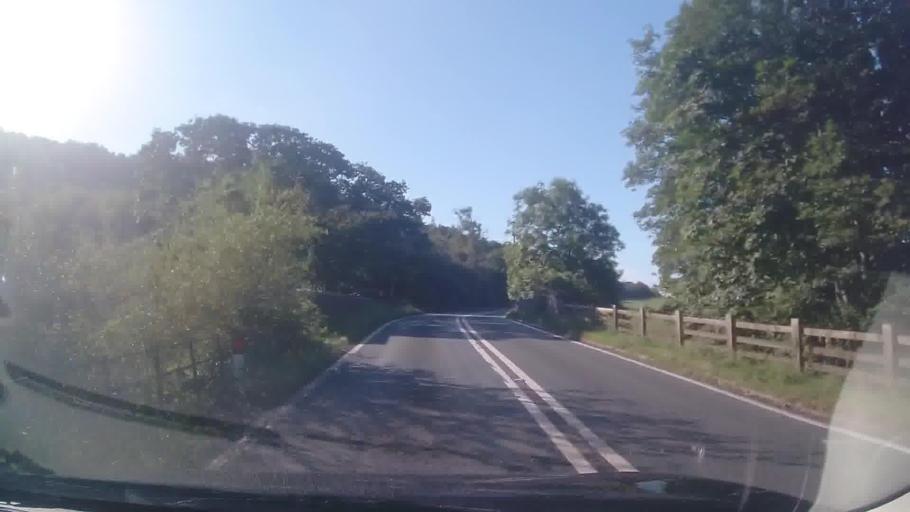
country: GB
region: England
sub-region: Cumbria
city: Seascale
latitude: 54.3667
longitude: -3.3951
